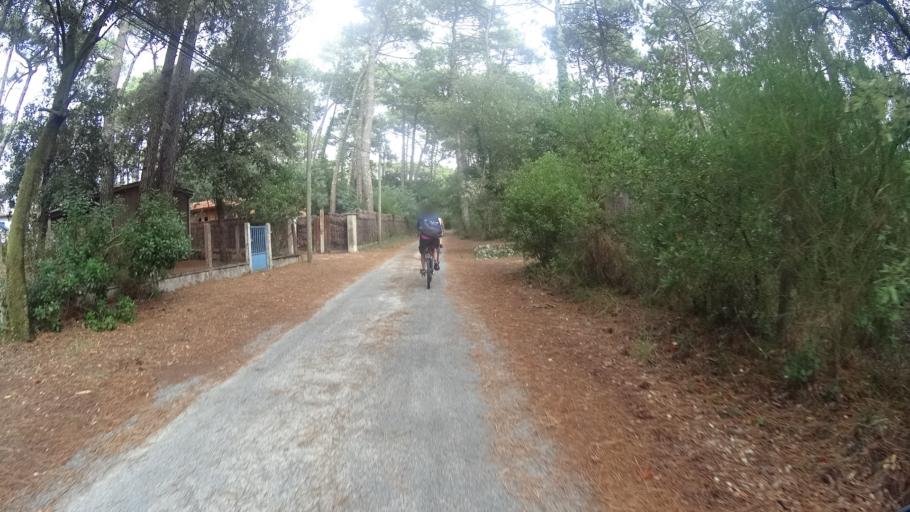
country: FR
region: Aquitaine
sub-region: Departement de la Gironde
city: Lacanau
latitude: 44.9902
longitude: -1.1417
